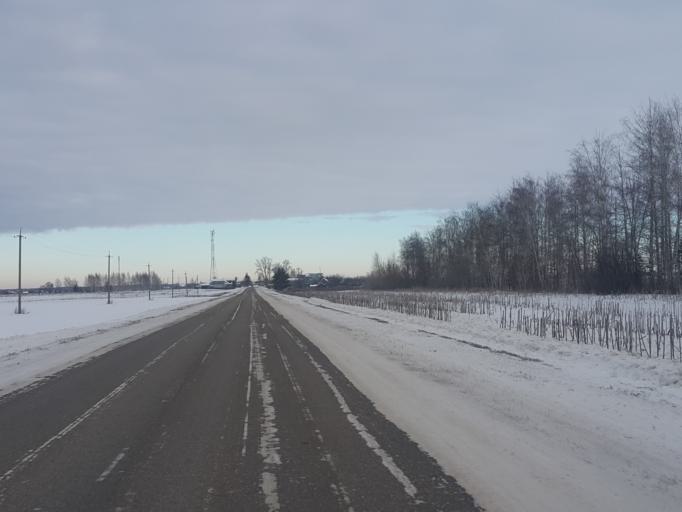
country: RU
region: Tambov
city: Rasskazovo
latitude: 52.8221
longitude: 41.8003
